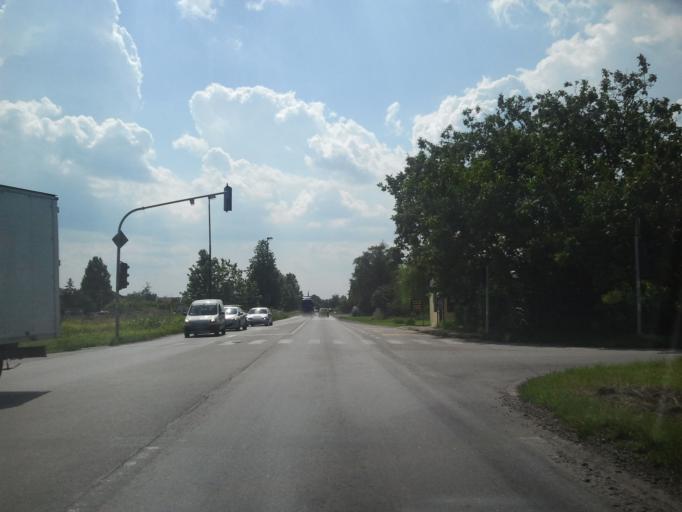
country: RS
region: Autonomna Pokrajina Vojvodina
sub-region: Juznobacki Okrug
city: Beocin
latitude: 45.2427
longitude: 19.7191
